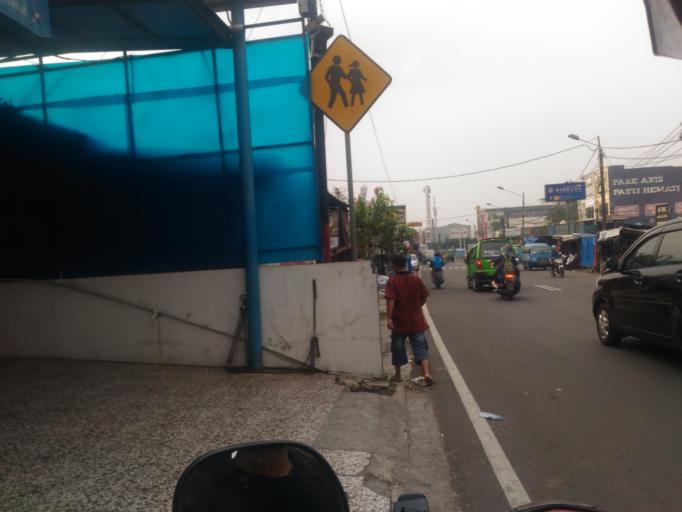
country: ID
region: West Java
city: Caringin
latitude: -6.6485
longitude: 106.8433
